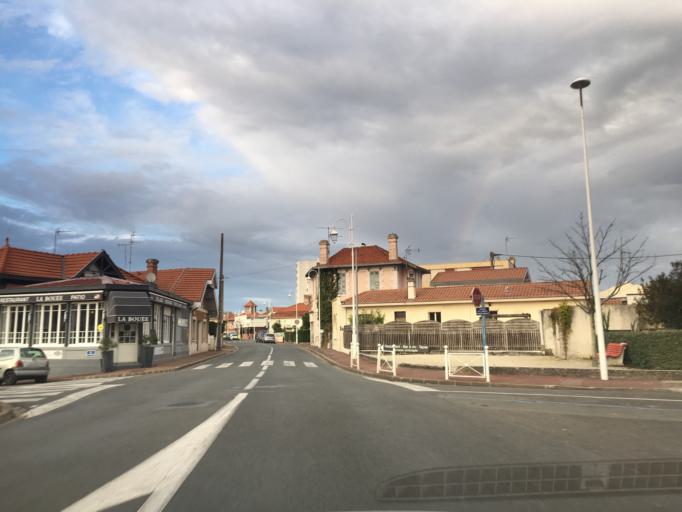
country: FR
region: Aquitaine
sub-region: Departement de la Gironde
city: Arcachon
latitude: 44.6544
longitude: -1.1464
